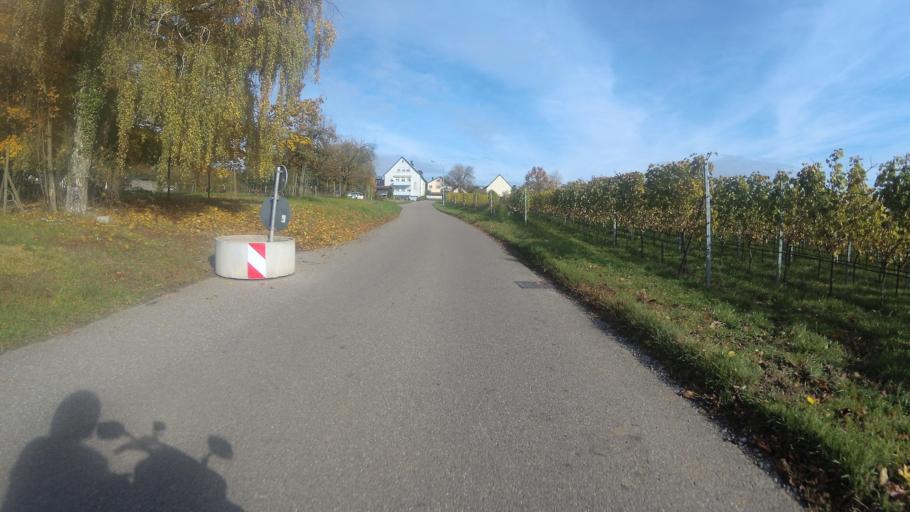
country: DE
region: Baden-Wuerttemberg
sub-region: Regierungsbezirk Stuttgart
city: Oedheim
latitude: 49.2555
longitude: 9.2613
